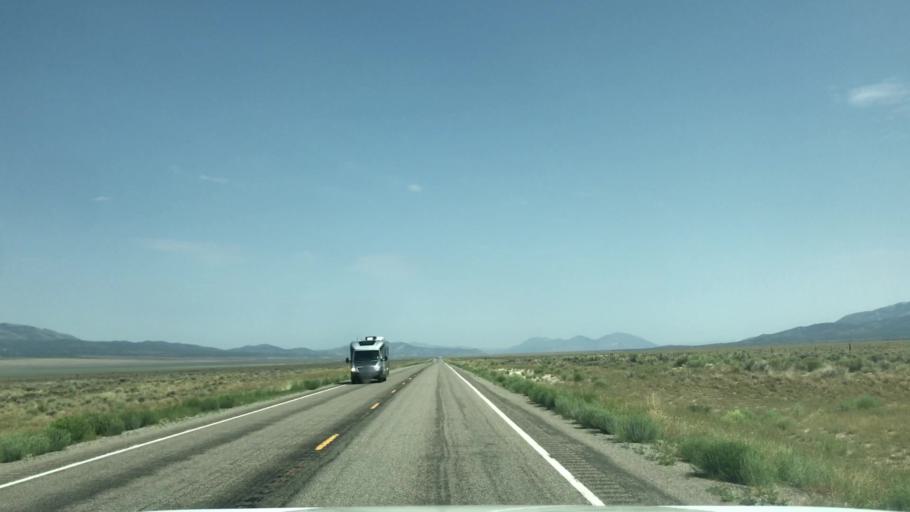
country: US
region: Nevada
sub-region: White Pine County
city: Ely
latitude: 39.0691
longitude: -114.7380
